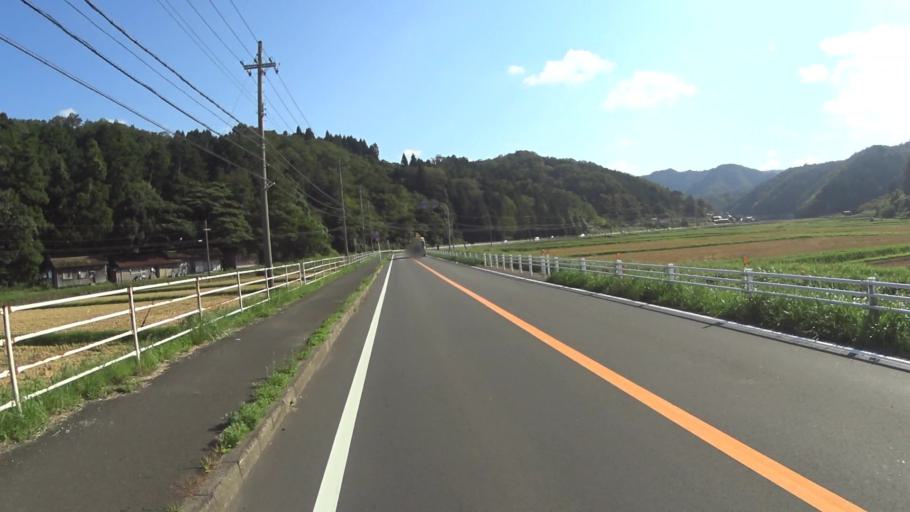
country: JP
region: Kyoto
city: Miyazu
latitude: 35.6643
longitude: 135.0236
